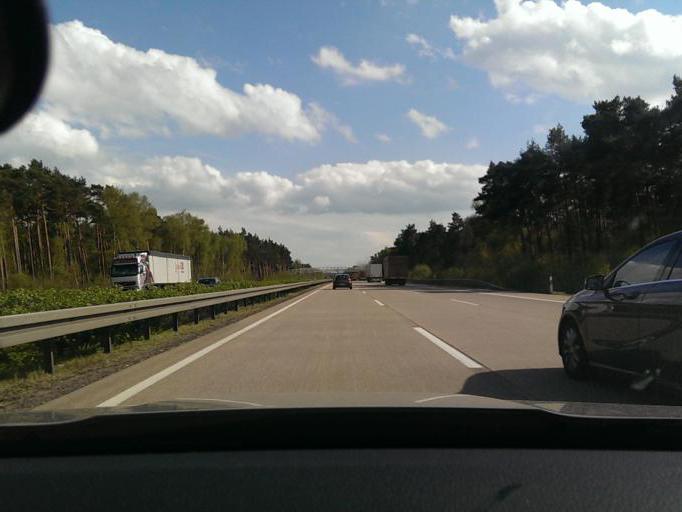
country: DE
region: Lower Saxony
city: Isernhagen Farster Bauerschaft
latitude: 52.5179
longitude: 9.8177
